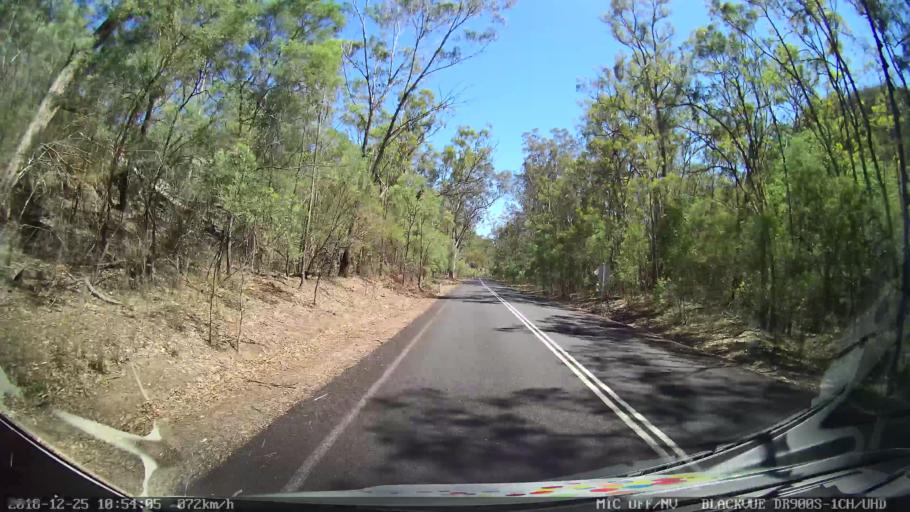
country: AU
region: New South Wales
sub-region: Upper Hunter Shire
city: Merriwa
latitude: -32.4137
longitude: 150.2730
